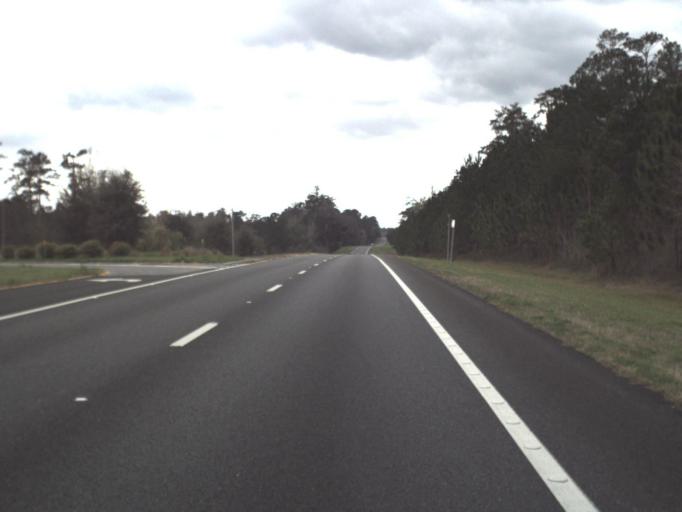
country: US
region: Florida
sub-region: Leon County
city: Tallahassee
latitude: 30.6062
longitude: -84.1797
